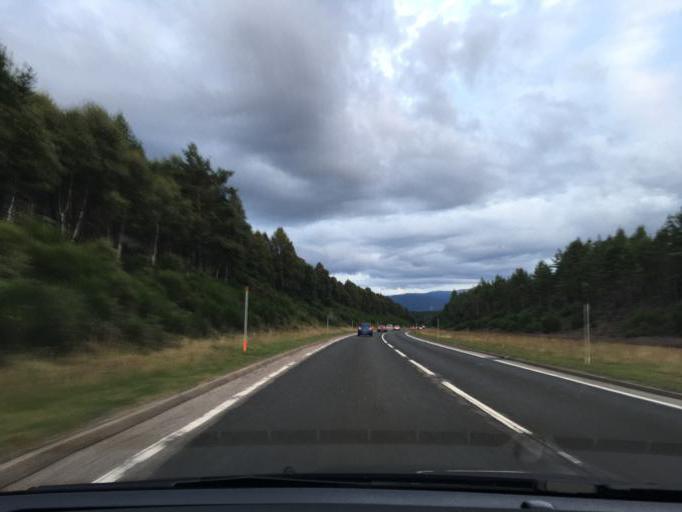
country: GB
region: Scotland
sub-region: Highland
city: Aviemore
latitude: 57.2896
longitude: -3.8468
